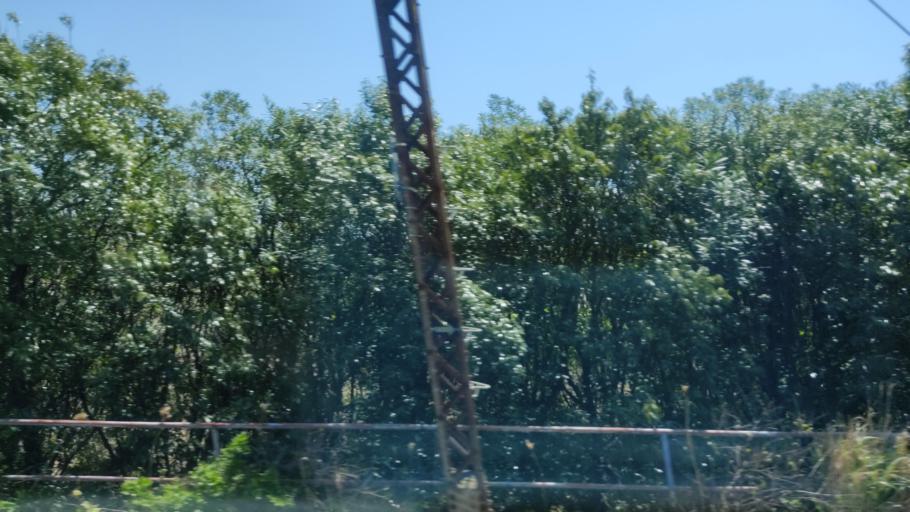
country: JP
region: Kanagawa
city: Hiratsuka
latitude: 35.3188
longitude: 139.3249
